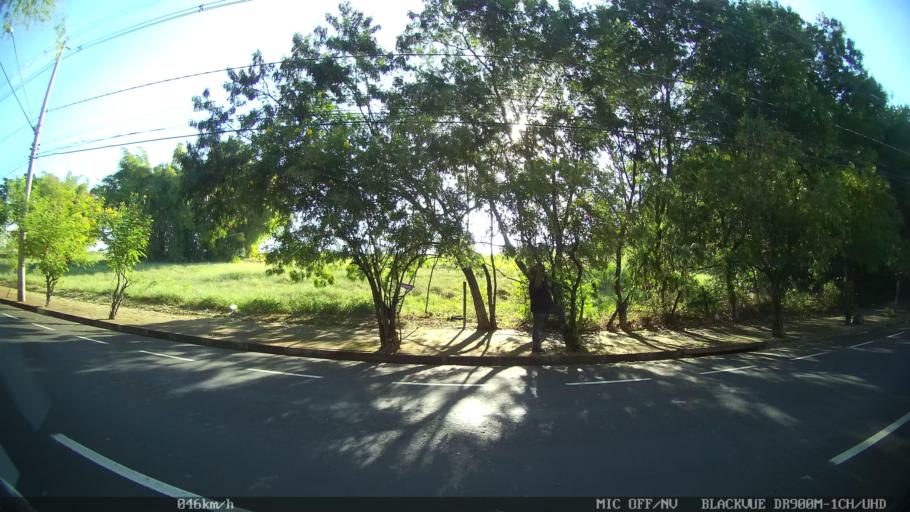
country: BR
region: Sao Paulo
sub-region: Sao Jose Do Rio Preto
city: Sao Jose do Rio Preto
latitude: -20.8412
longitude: -49.4112
